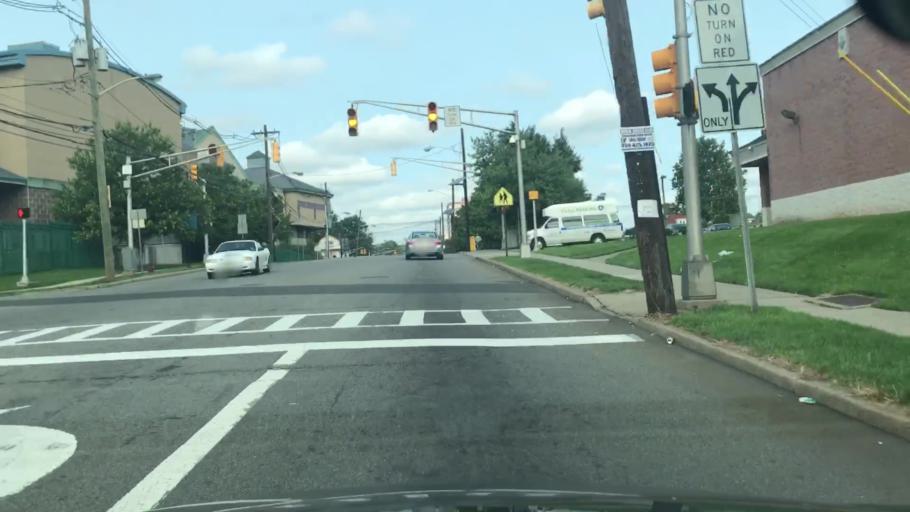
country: US
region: New Jersey
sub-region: Union County
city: Elizabeth
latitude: 40.6812
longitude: -74.2064
